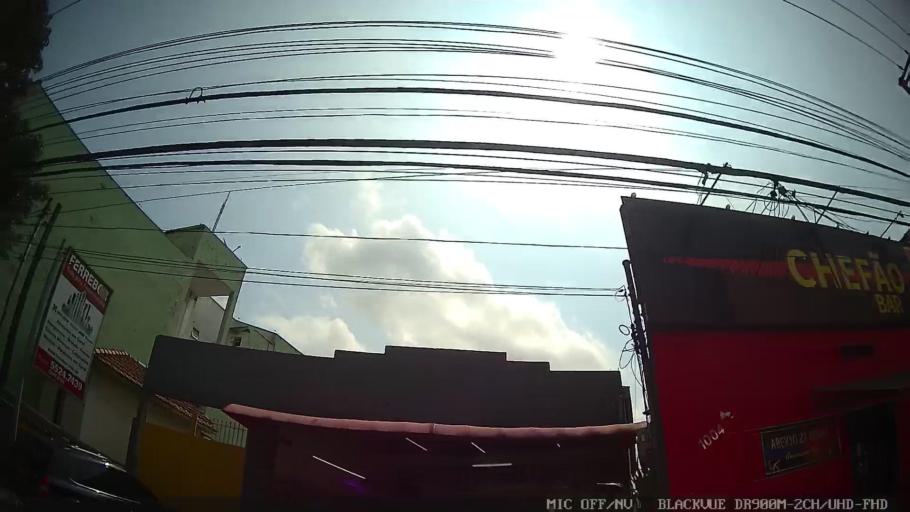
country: BR
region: Sao Paulo
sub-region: Taboao Da Serra
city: Taboao da Serra
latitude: -23.6462
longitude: -46.7106
